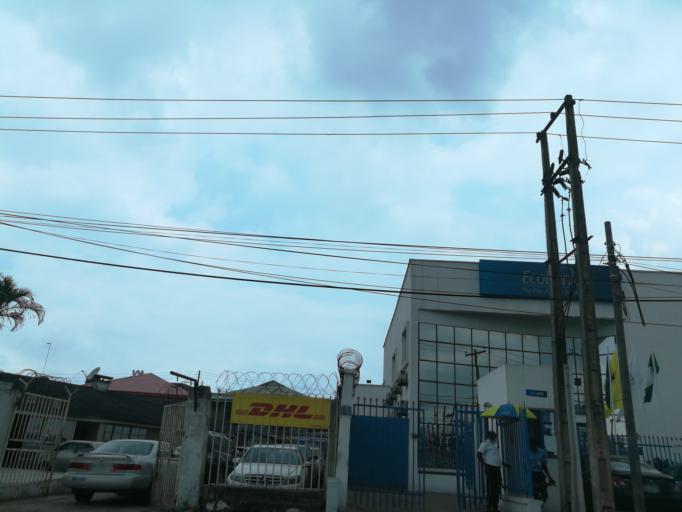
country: NG
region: Lagos
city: Ikeja
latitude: 6.6001
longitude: 3.3392
